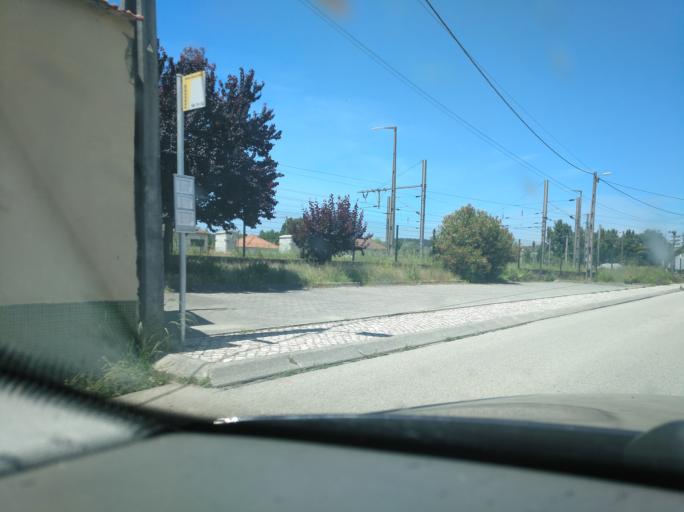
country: PT
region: Aveiro
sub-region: Mealhada
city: Pampilhosa do Botao
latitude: 40.2868
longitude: -8.4249
